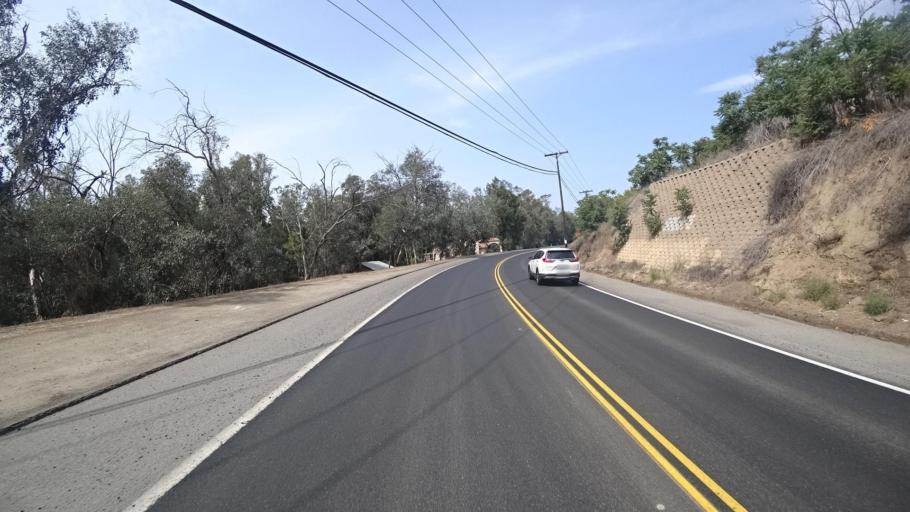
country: US
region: California
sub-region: San Diego County
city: Escondido
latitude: 33.1095
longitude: -117.0543
